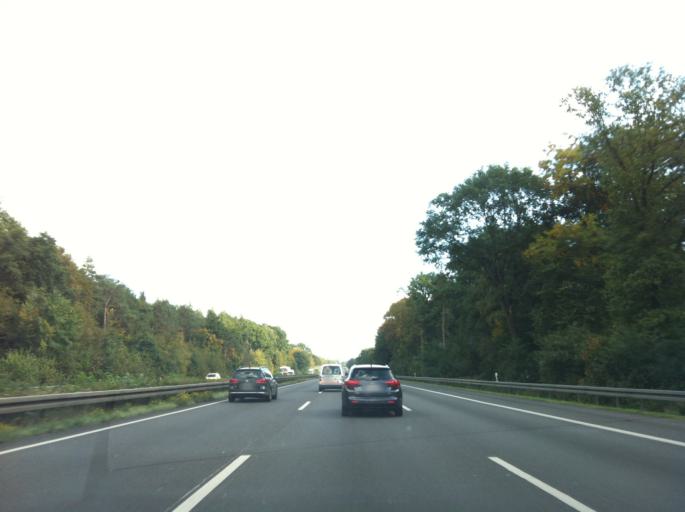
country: DE
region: North Rhine-Westphalia
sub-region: Regierungsbezirk Koln
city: Rosrath
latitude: 50.9028
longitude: 7.1365
